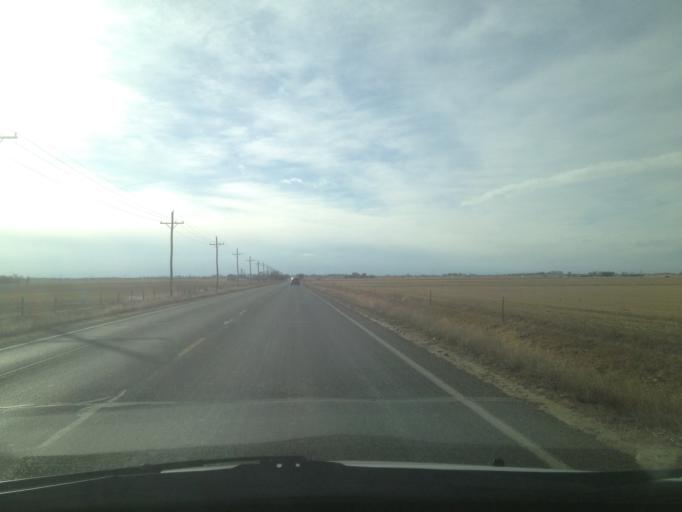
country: US
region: Colorado
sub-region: Weld County
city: Hudson
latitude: 40.0806
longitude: -104.6683
